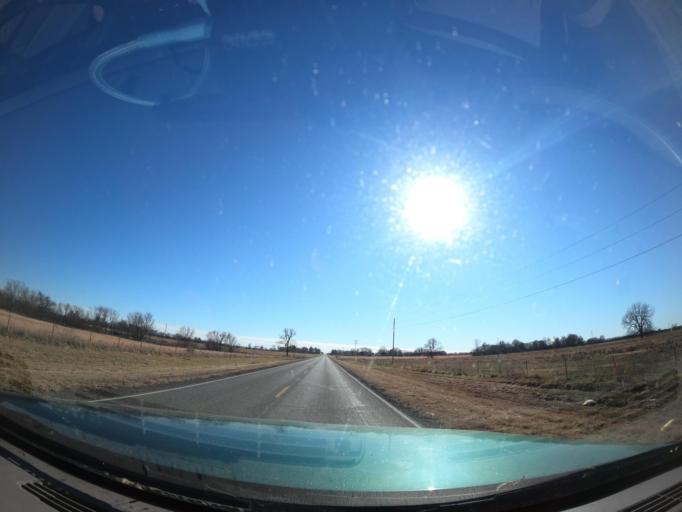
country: US
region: Oklahoma
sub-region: Muskogee County
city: Haskell
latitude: 35.6982
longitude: -95.6423
